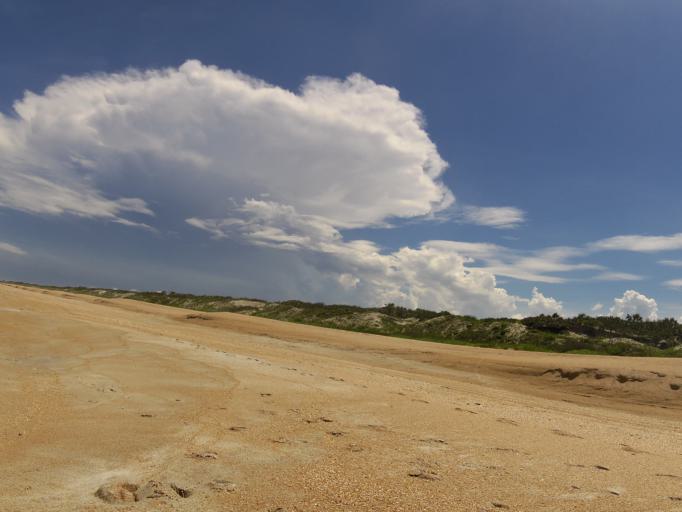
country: US
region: Florida
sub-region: Saint Johns County
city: Palm Valley
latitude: 30.1104
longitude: -81.3431
